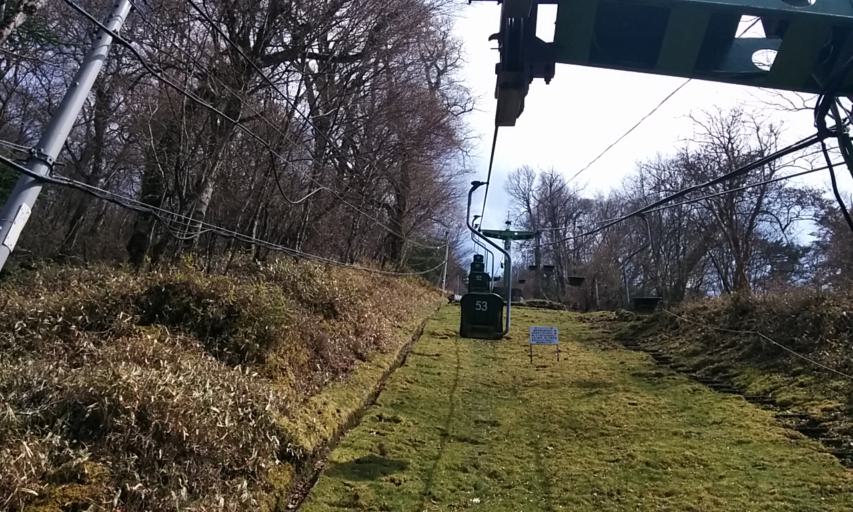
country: JP
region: Tokushima
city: Wakimachi
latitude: 33.8659
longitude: 134.0894
